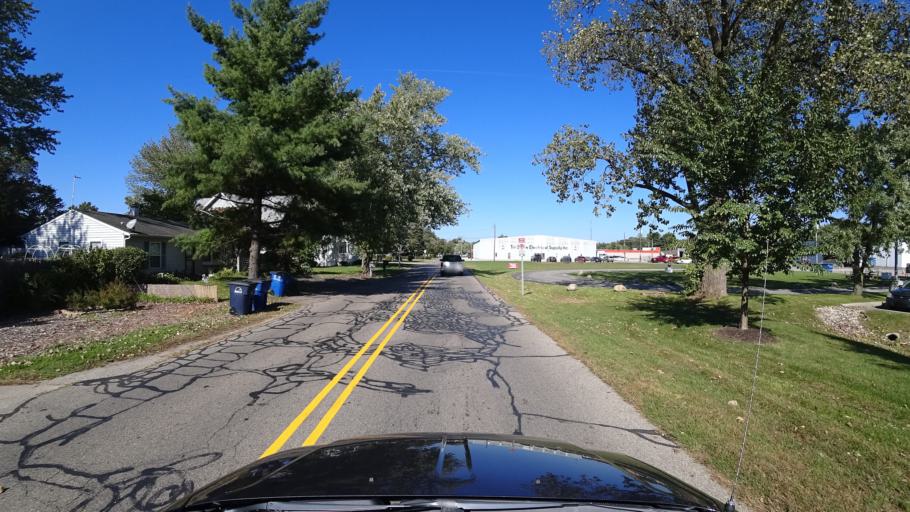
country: US
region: Indiana
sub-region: LaPorte County
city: Michigan City
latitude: 41.6909
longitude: -86.8952
